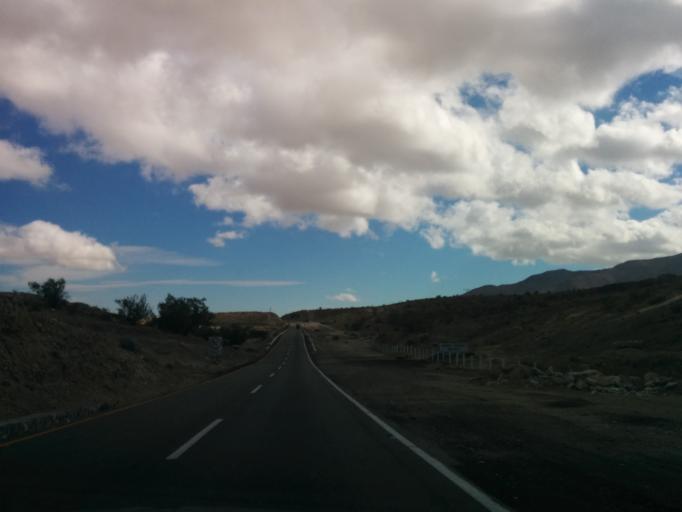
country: MX
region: Baja California
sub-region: Tecate
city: Cereso del Hongo
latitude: 32.5660
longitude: -115.9551
